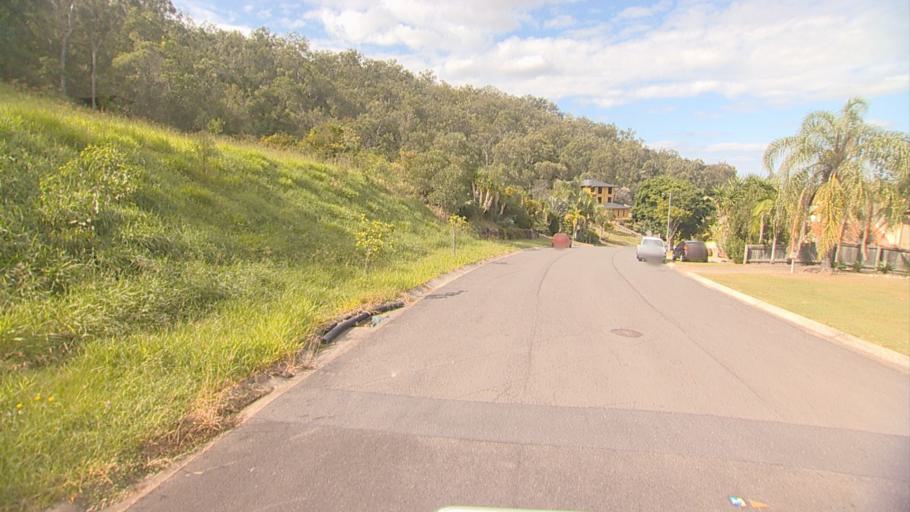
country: AU
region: Queensland
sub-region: Logan
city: Windaroo
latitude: -27.7301
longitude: 153.1969
